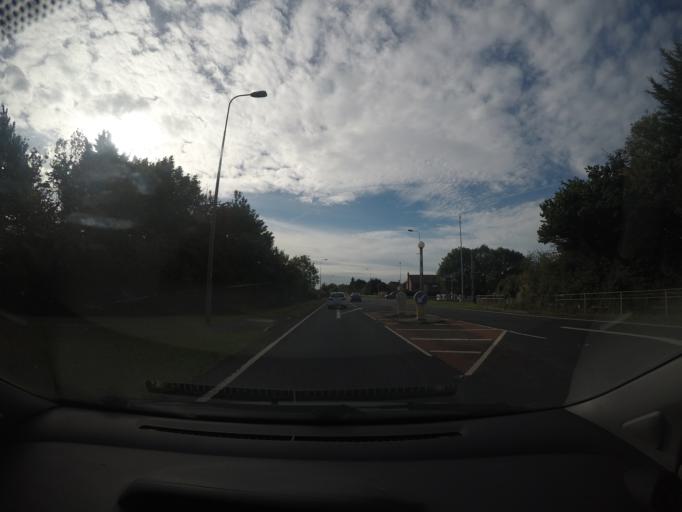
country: GB
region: England
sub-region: North Yorkshire
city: Riccall
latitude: 53.8384
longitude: -1.0554
